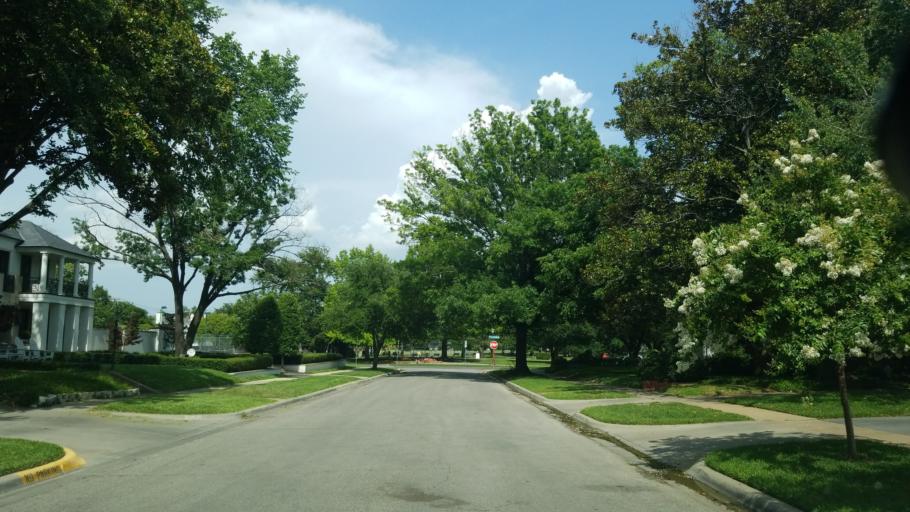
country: US
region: Texas
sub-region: Dallas County
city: University Park
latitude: 32.8581
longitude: -96.7905
